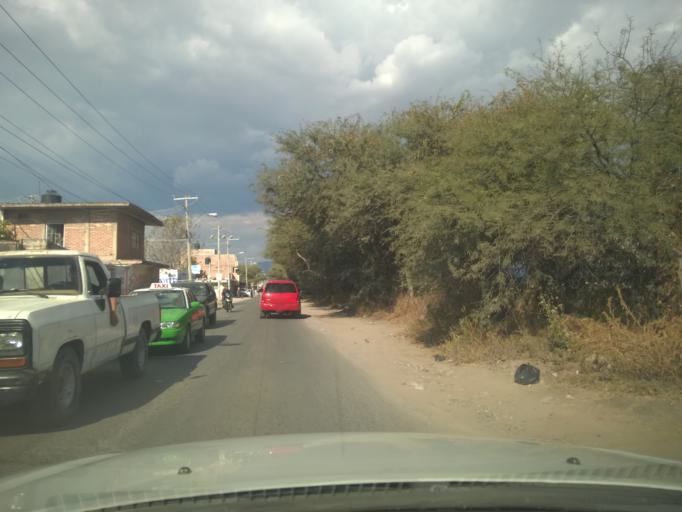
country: MX
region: Guanajuato
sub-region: Leon
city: San Jose de Duran (Los Troncoso)
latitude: 21.0642
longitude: -101.6259
